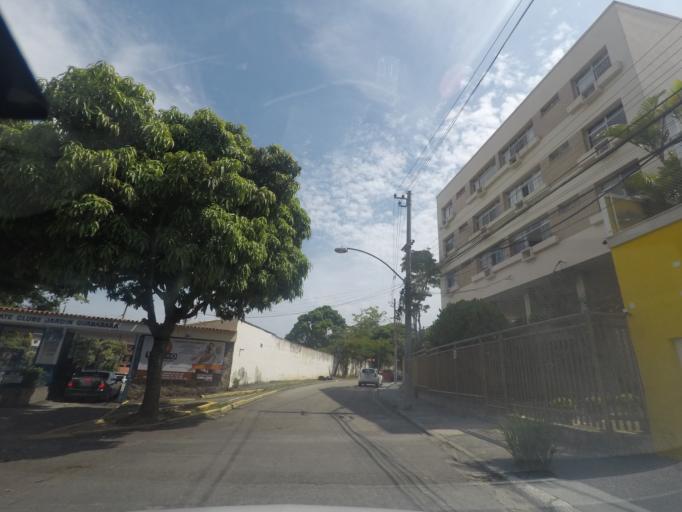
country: BR
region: Rio de Janeiro
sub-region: Rio De Janeiro
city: Rio de Janeiro
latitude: -22.8136
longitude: -43.2077
